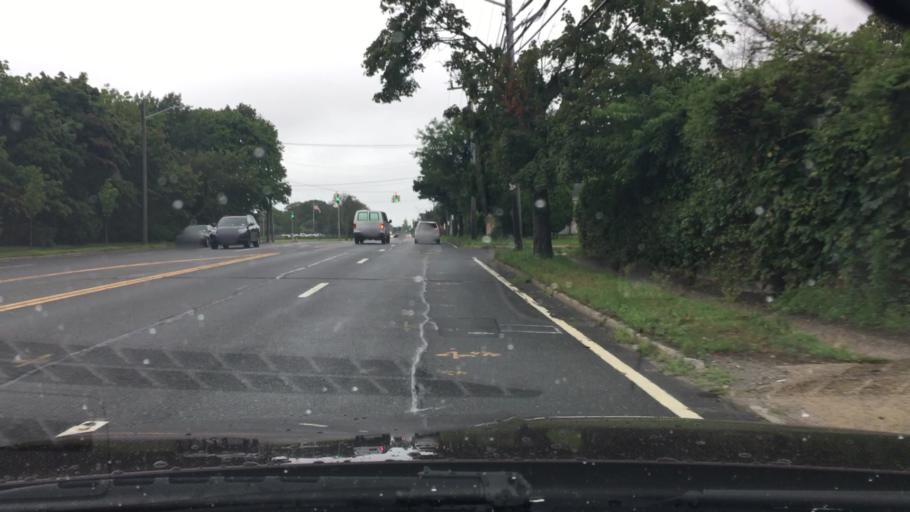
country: US
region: New York
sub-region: Nassau County
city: Hicksville
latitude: 40.7675
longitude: -73.5082
